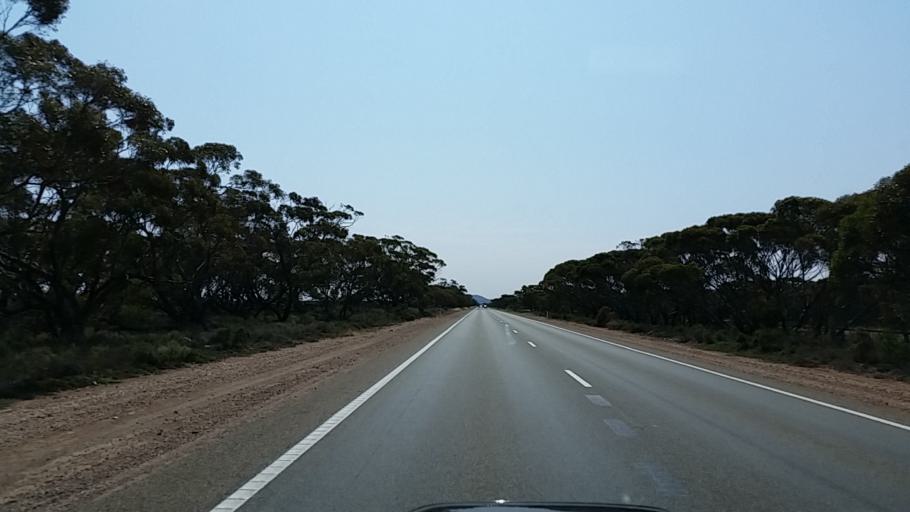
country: AU
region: South Australia
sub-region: Port Pirie City and Dists
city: Port Pirie
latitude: -32.9397
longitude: 137.9824
